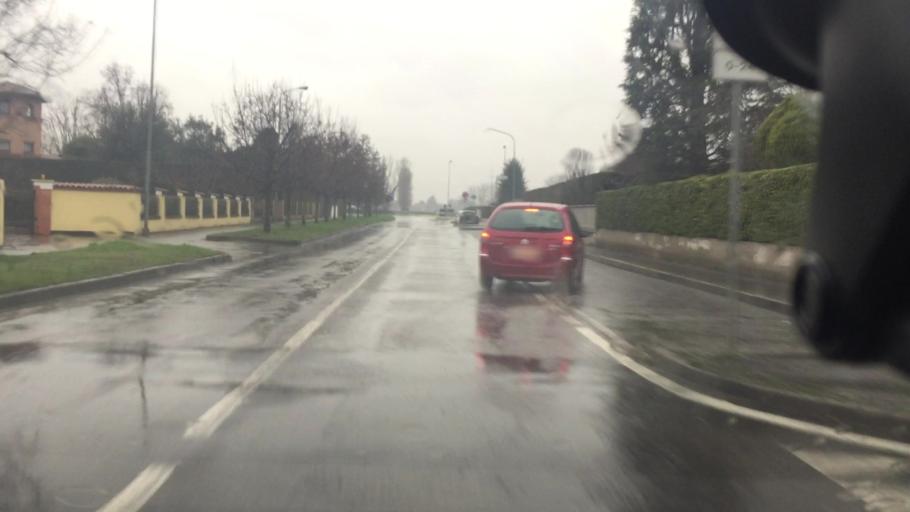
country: IT
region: Lombardy
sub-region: Citta metropolitana di Milano
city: Vaprio d'Adda
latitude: 45.5812
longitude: 9.5230
